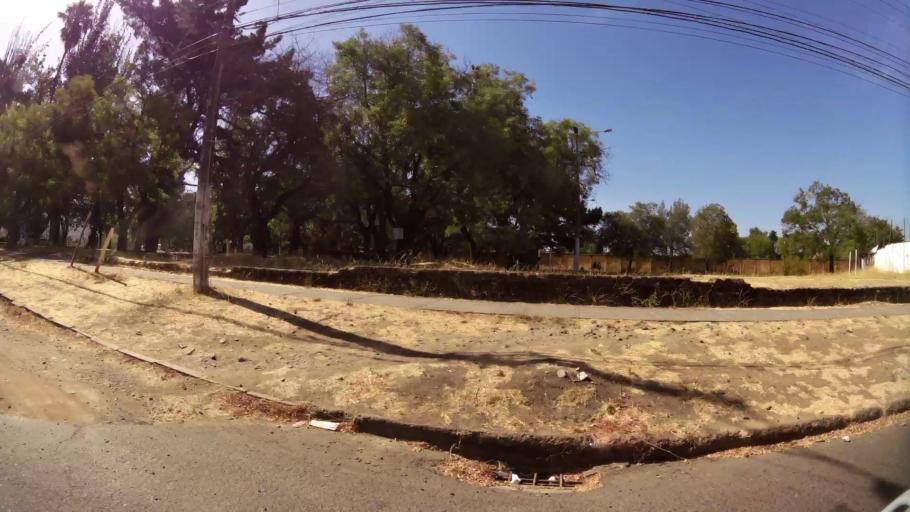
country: CL
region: Maule
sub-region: Provincia de Talca
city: Talca
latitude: -35.4167
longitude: -71.6639
